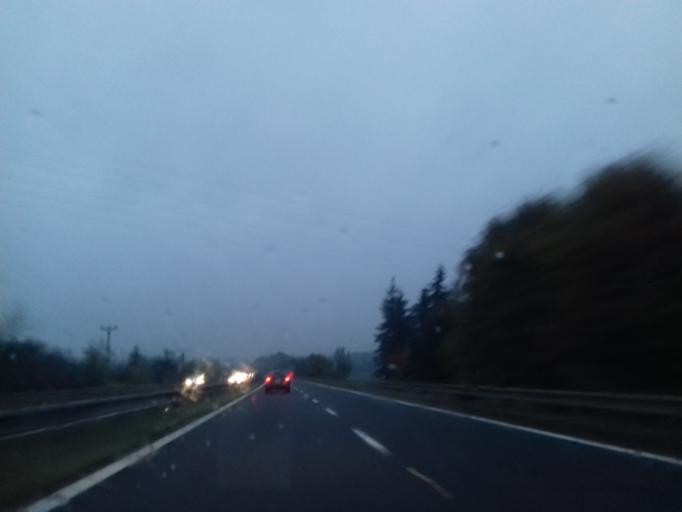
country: CZ
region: Olomoucky
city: Litovel
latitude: 49.6958
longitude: 17.0445
